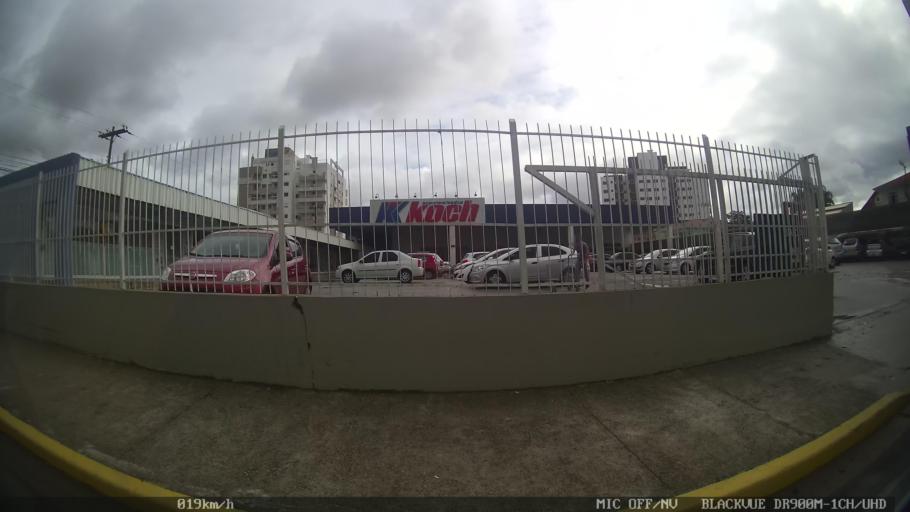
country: BR
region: Santa Catarina
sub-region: Biguacu
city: Biguacu
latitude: -27.5079
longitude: -48.6515
